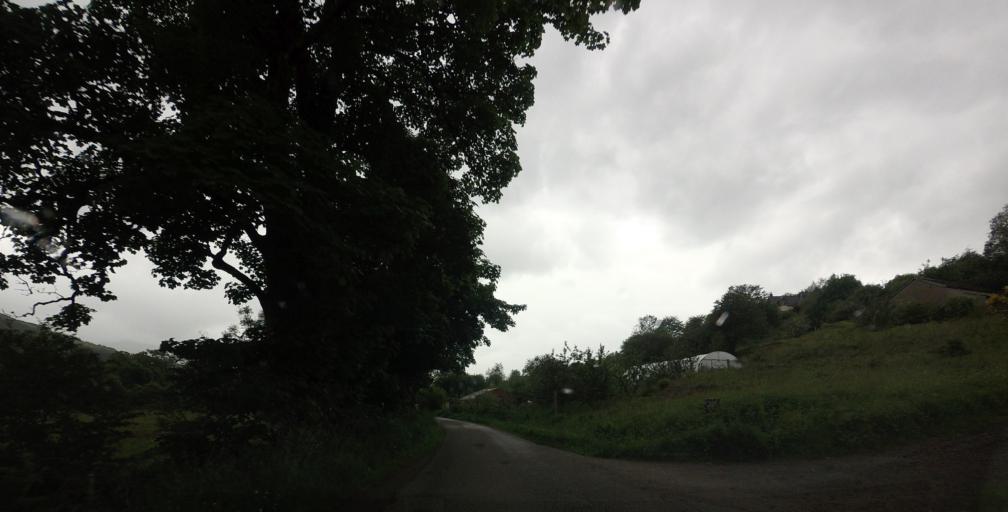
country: GB
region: Scotland
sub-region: Argyll and Bute
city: Oban
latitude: 56.7040
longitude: -5.5700
